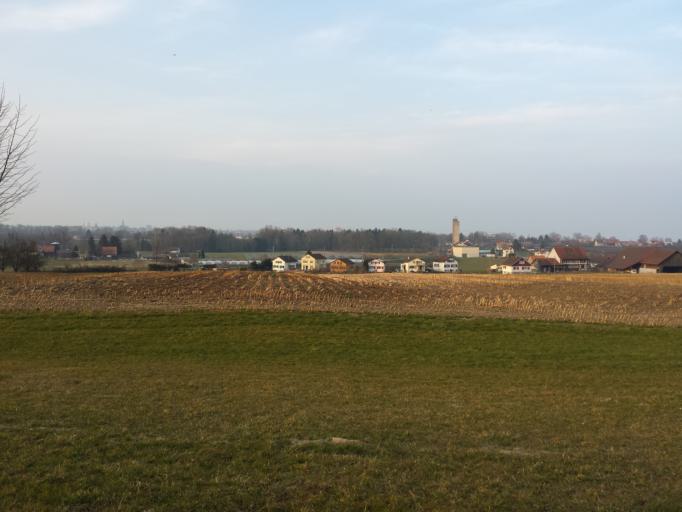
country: CH
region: Thurgau
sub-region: Arbon District
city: Egnach
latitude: 47.5320
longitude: 9.3706
